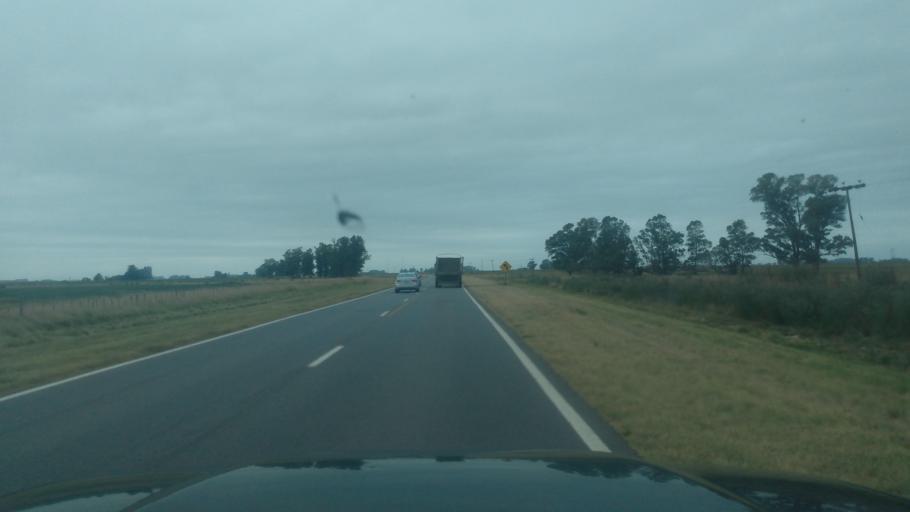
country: AR
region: Buenos Aires
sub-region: Partido de Nueve de Julio
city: Nueve de Julio
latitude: -35.3979
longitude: -60.7509
